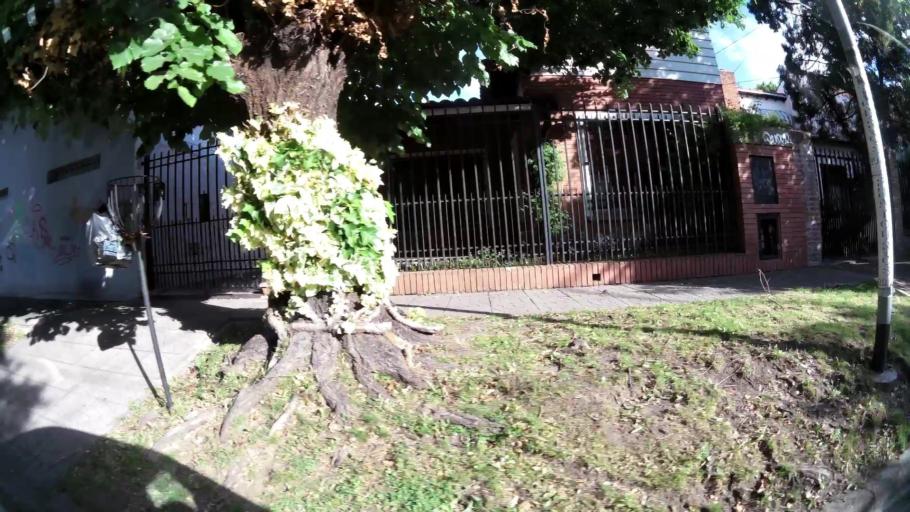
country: AR
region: Buenos Aires
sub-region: Partido de General San Martin
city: General San Martin
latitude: -34.5478
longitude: -58.5593
